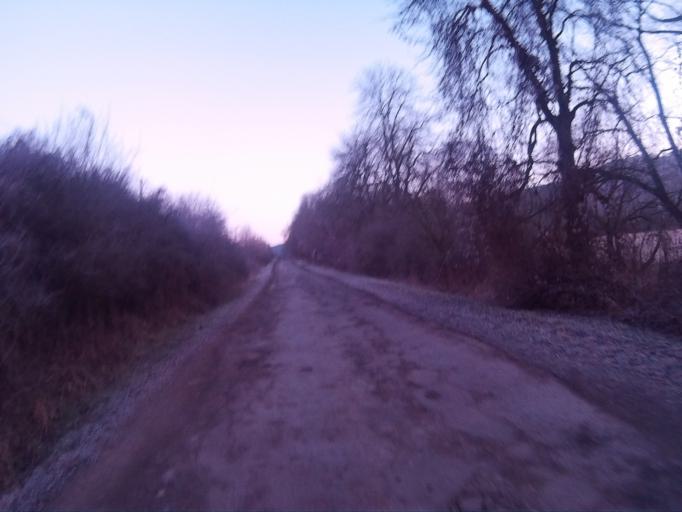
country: HU
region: Borsod-Abauj-Zemplen
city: Putnok
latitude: 48.3088
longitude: 20.4382
